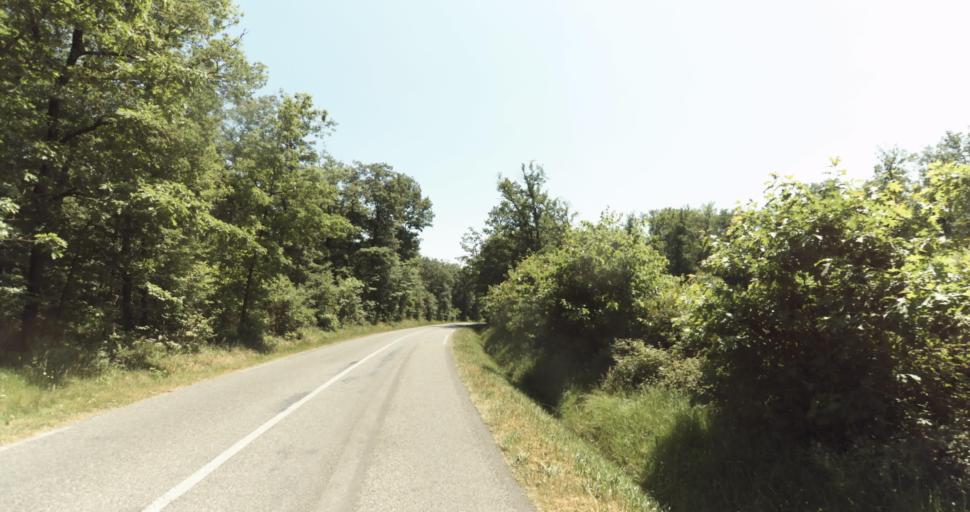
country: FR
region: Midi-Pyrenees
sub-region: Departement de la Haute-Garonne
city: Levignac
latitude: 43.6221
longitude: 1.1893
